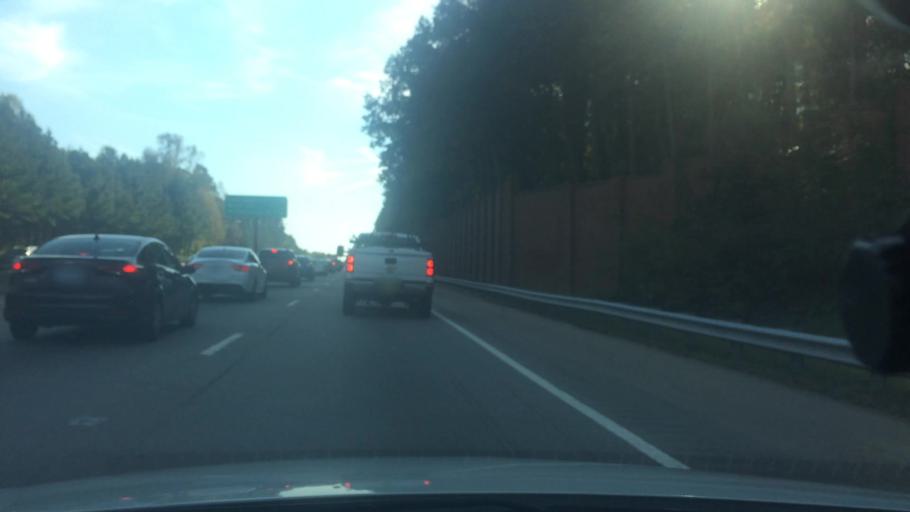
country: US
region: North Carolina
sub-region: Wake County
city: West Raleigh
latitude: 35.8227
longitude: -78.6863
